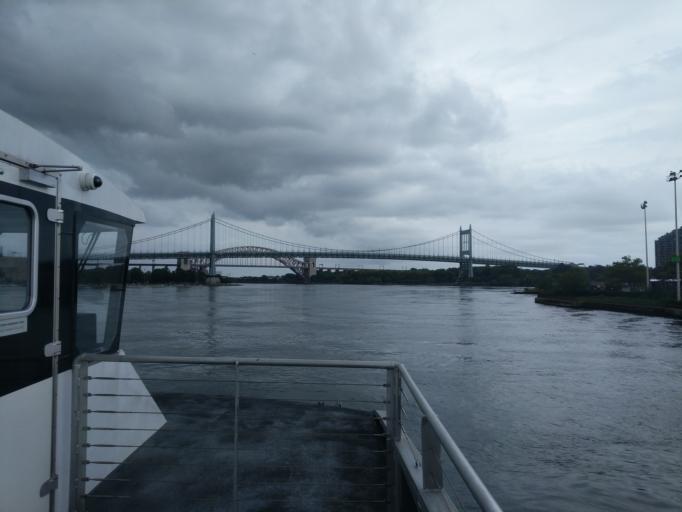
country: US
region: New York
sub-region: New York County
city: Manhattan
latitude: 40.7784
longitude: -73.9361
